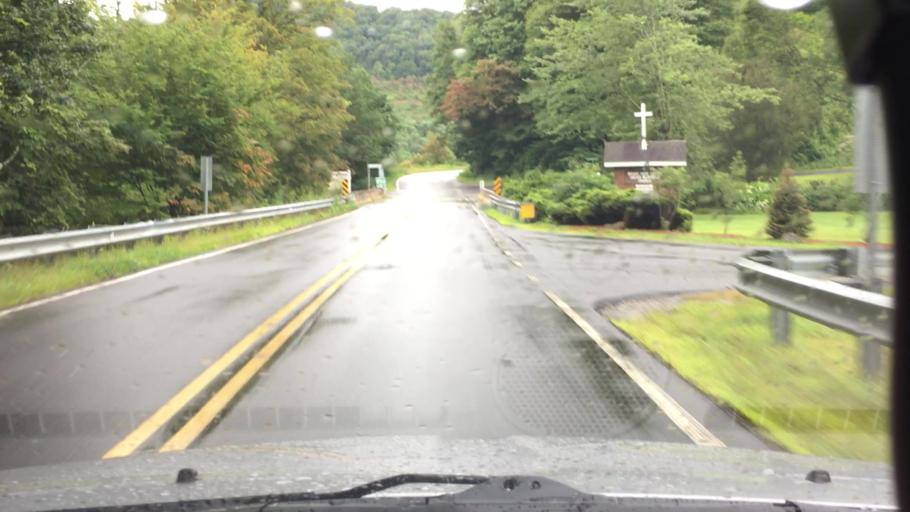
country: US
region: North Carolina
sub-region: Madison County
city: Mars Hill
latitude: 35.9102
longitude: -82.5435
